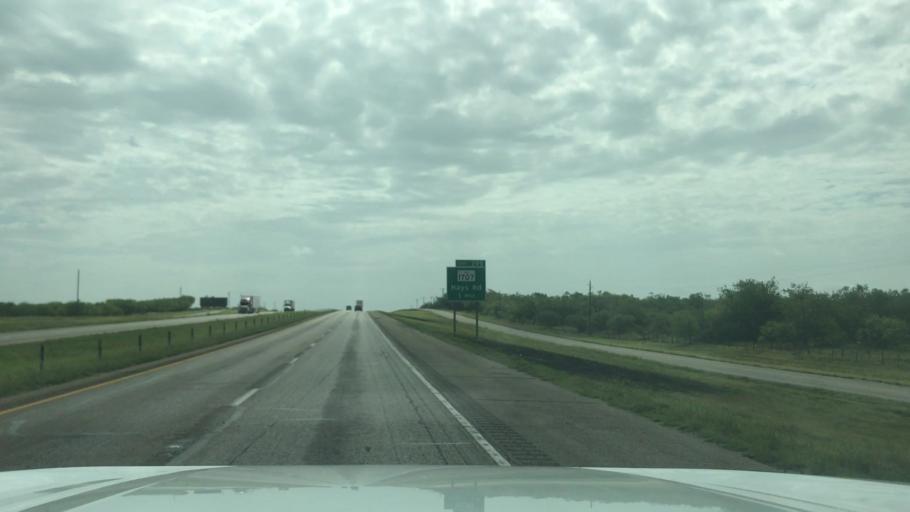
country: US
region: Texas
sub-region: Callahan County
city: Clyde
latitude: 32.4222
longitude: -99.5487
